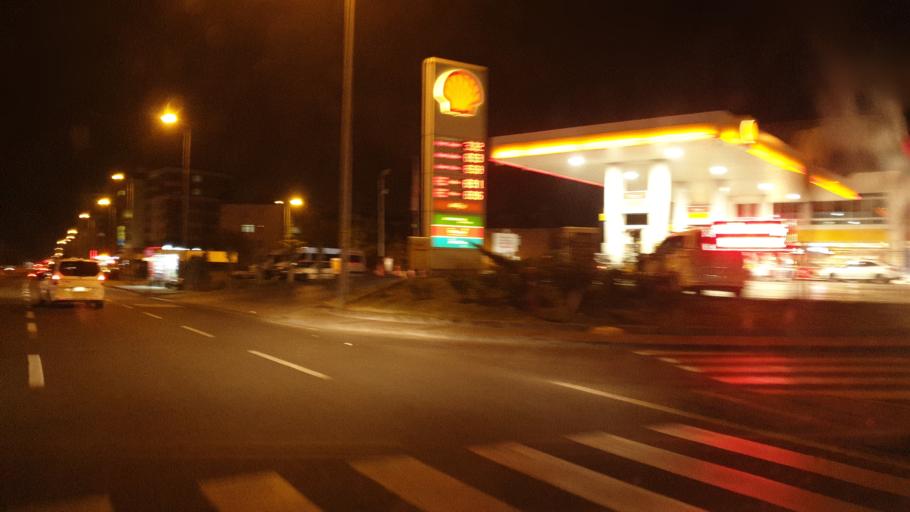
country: TR
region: Kayseri
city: Talas
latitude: 38.6940
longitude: 35.5459
